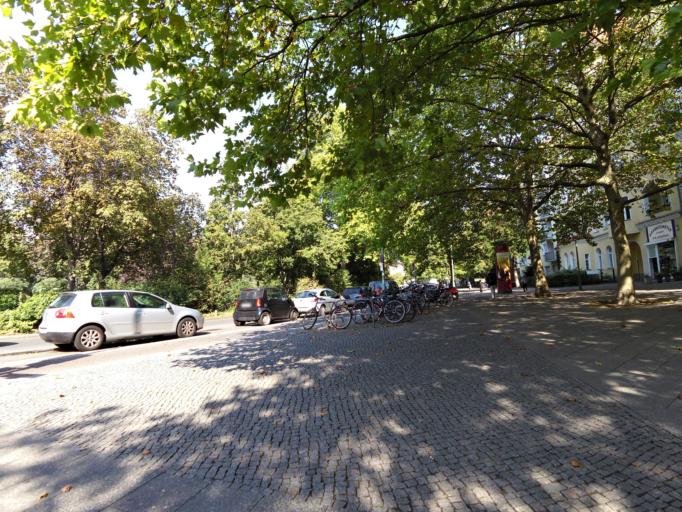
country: DE
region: Berlin
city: Friedenau
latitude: 52.4790
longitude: 13.3291
